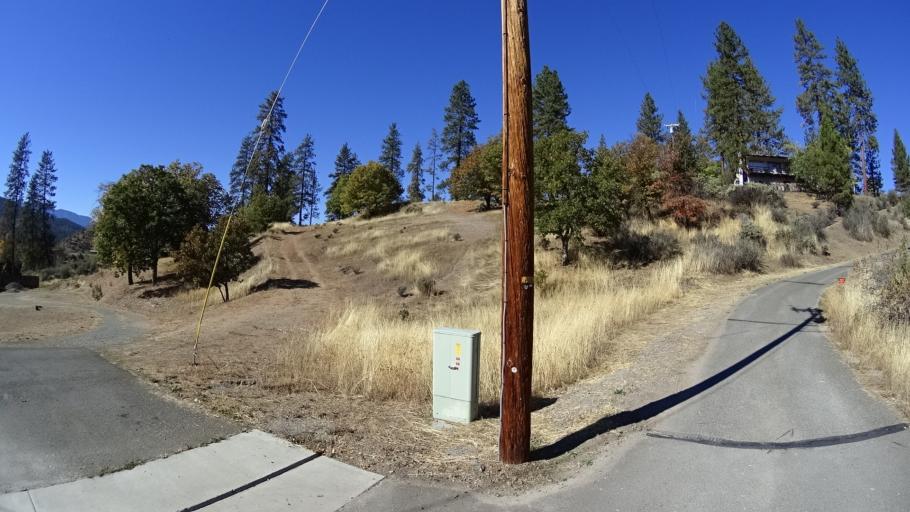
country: US
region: California
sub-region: Siskiyou County
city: Yreka
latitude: 41.6083
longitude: -122.8377
